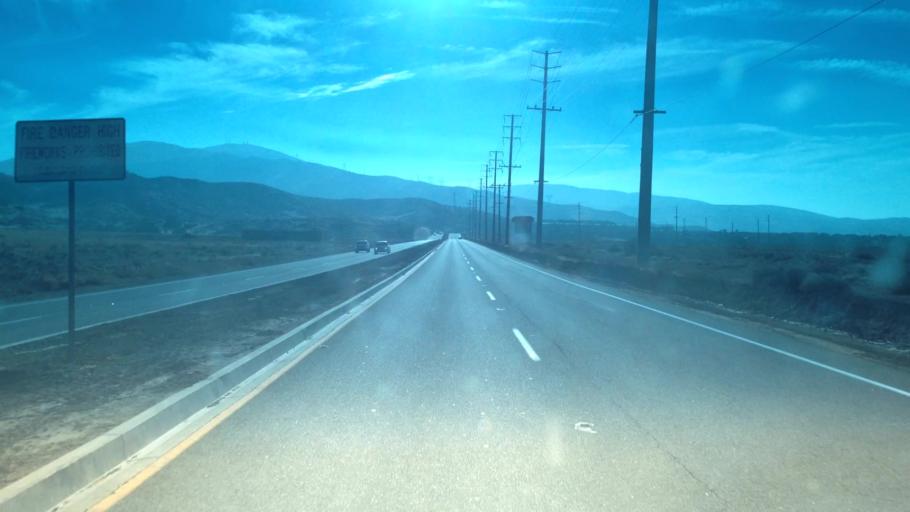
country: US
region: California
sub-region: Los Angeles County
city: Desert View Highlands
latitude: 34.5582
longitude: -118.1530
